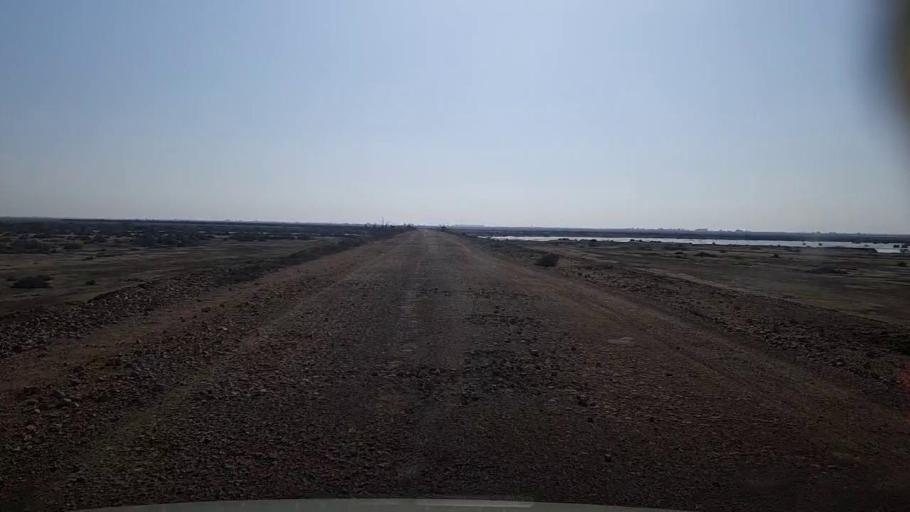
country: PK
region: Sindh
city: Mirpur Sakro
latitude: 24.5189
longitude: 67.4911
